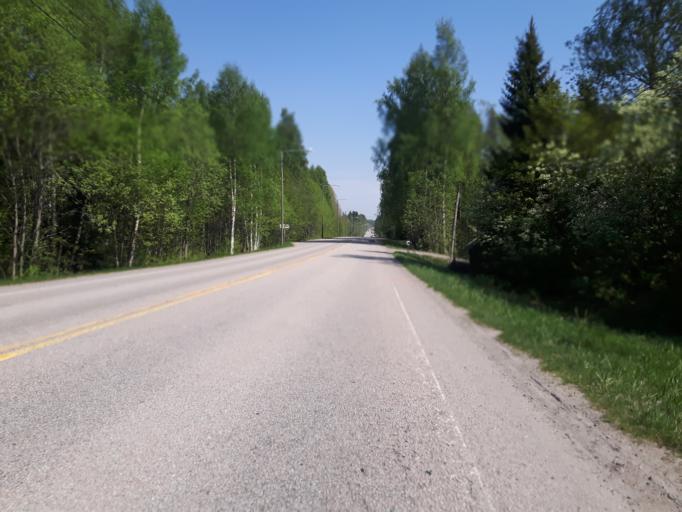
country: FI
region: Uusimaa
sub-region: Helsinki
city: Nickby
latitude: 60.3005
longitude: 25.3628
